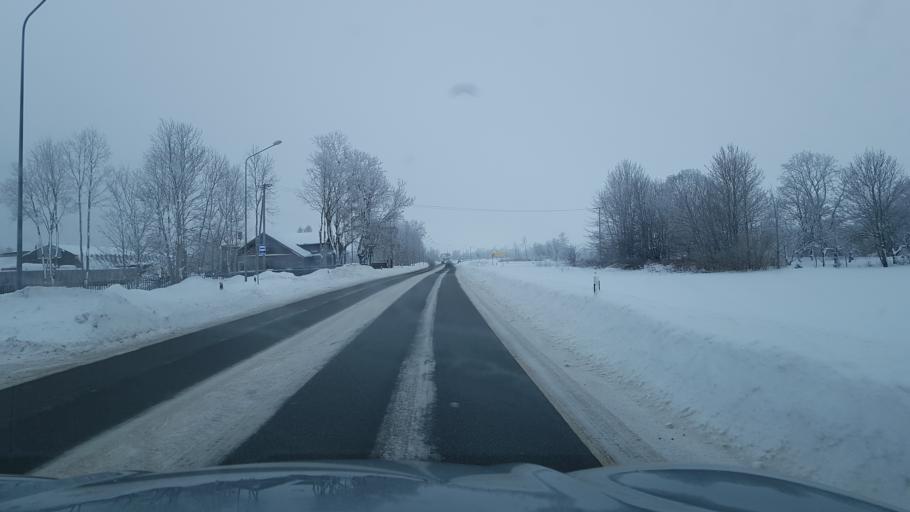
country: EE
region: Ida-Virumaa
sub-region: Johvi vald
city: Johvi
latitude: 59.3340
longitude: 27.4030
